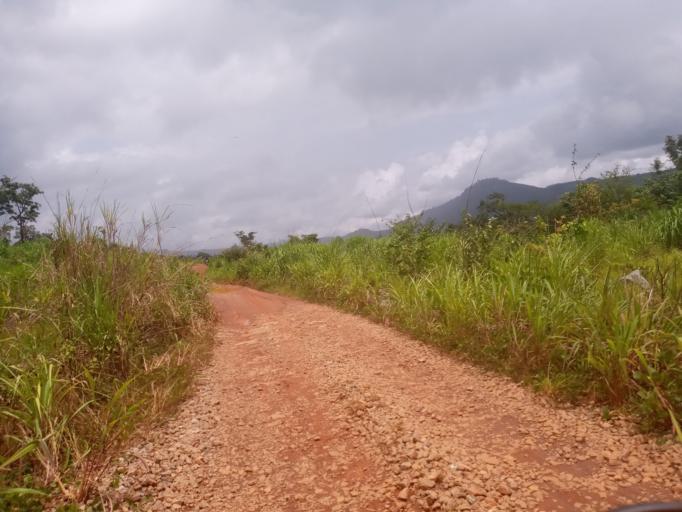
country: SL
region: Northern Province
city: Bumbuna
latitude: 8.9728
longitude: -11.7547
